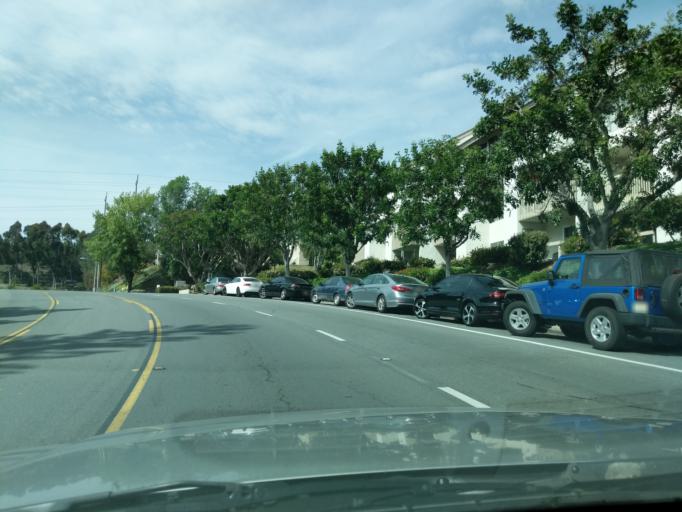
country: US
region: California
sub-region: San Diego County
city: San Diego
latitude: 32.7871
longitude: -117.1082
